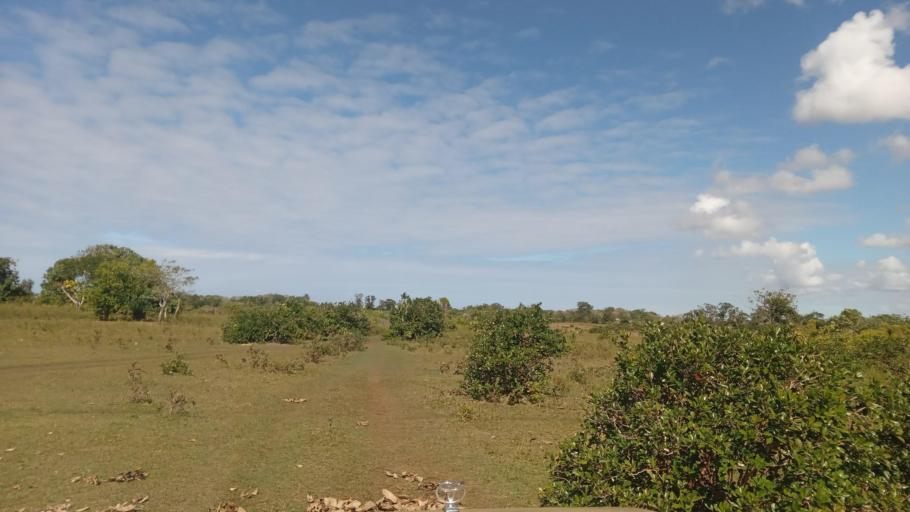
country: MG
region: Atsimo-Atsinanana
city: Vohipaho
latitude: -23.8323
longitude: 47.5534
